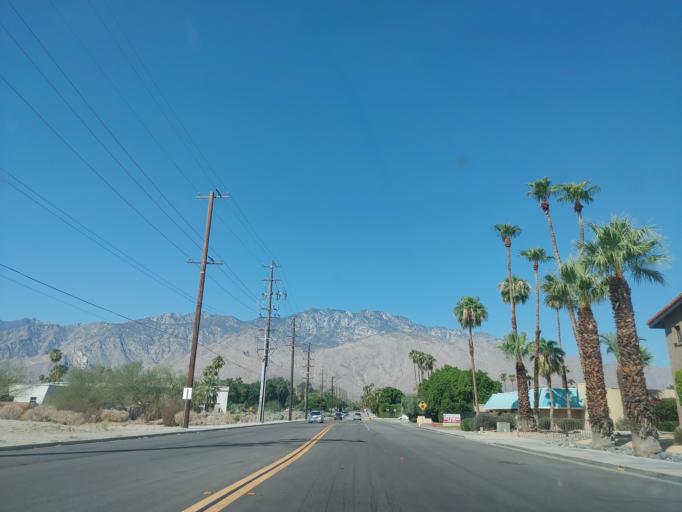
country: US
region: California
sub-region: Riverside County
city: Cathedral City
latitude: 33.8086
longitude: -116.4955
